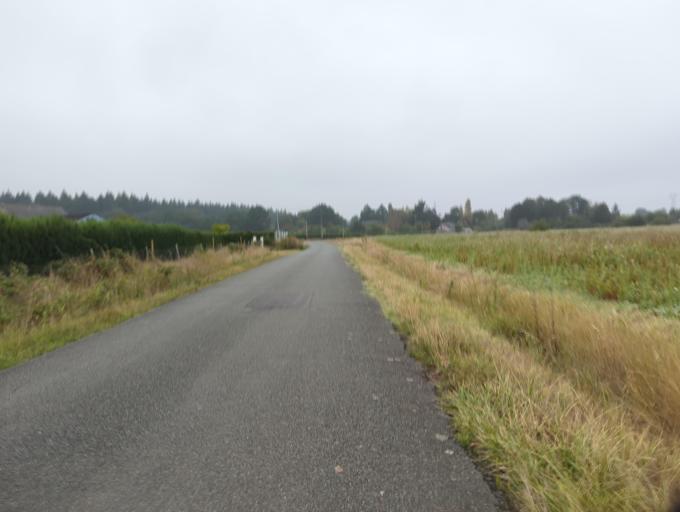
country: FR
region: Pays de la Loire
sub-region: Departement de Maine-et-Loire
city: Le Plessis-Grammoire
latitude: 47.4788
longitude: -0.4536
